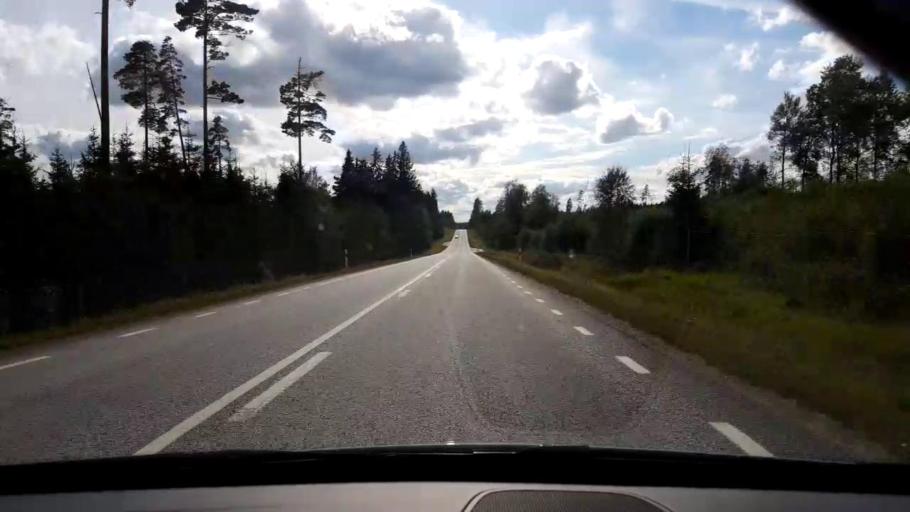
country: SE
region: Joenkoeping
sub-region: Savsjo Kommun
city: Stockaryd
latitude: 57.3758
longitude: 14.5483
